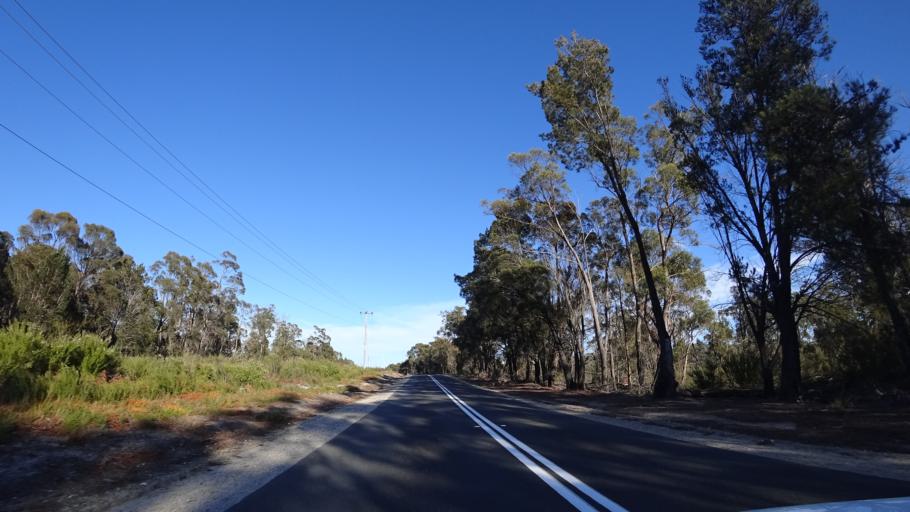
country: AU
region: Tasmania
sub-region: Break O'Day
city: St Helens
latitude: -41.2912
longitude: 148.1788
